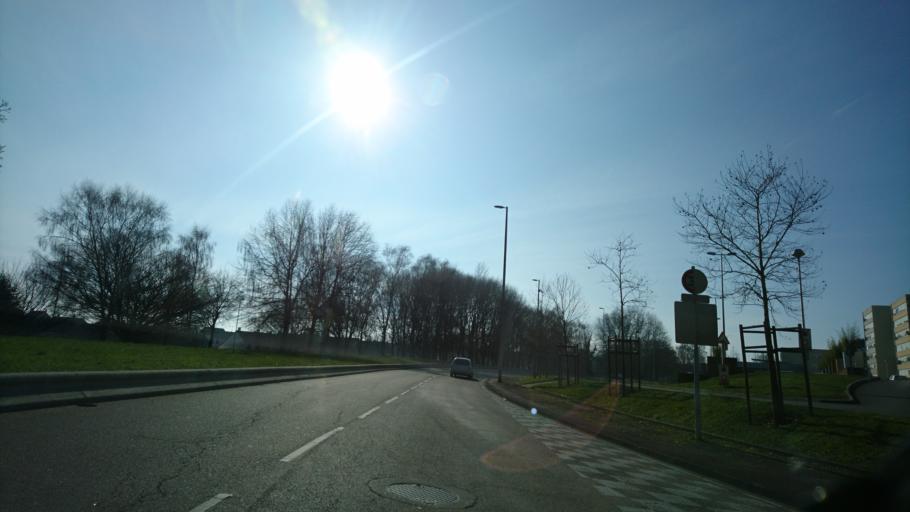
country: FR
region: Limousin
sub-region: Departement de la Haute-Vienne
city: Le Palais-sur-Vienne
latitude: 45.8780
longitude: 1.3005
